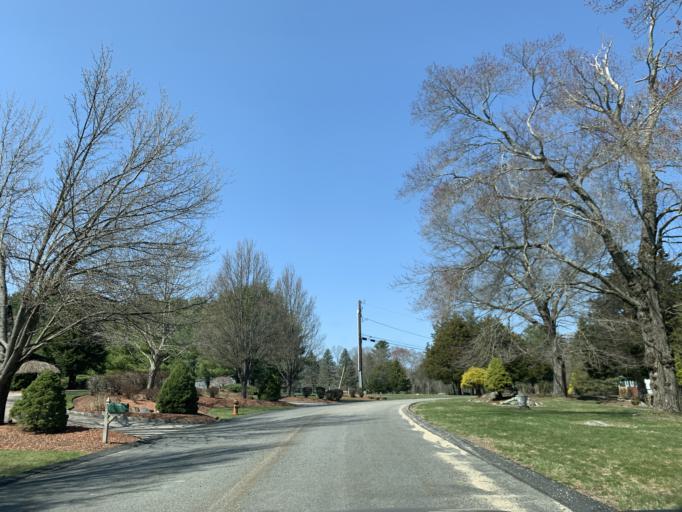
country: US
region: Rhode Island
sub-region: Kent County
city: East Greenwich
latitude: 41.6304
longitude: -71.4340
